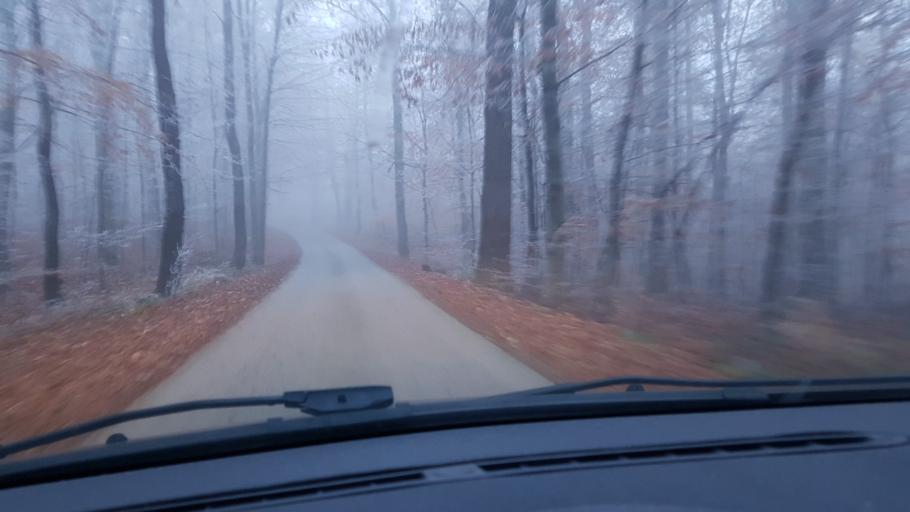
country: HR
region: Krapinsko-Zagorska
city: Pregrada
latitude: 46.1991
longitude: 15.7538
